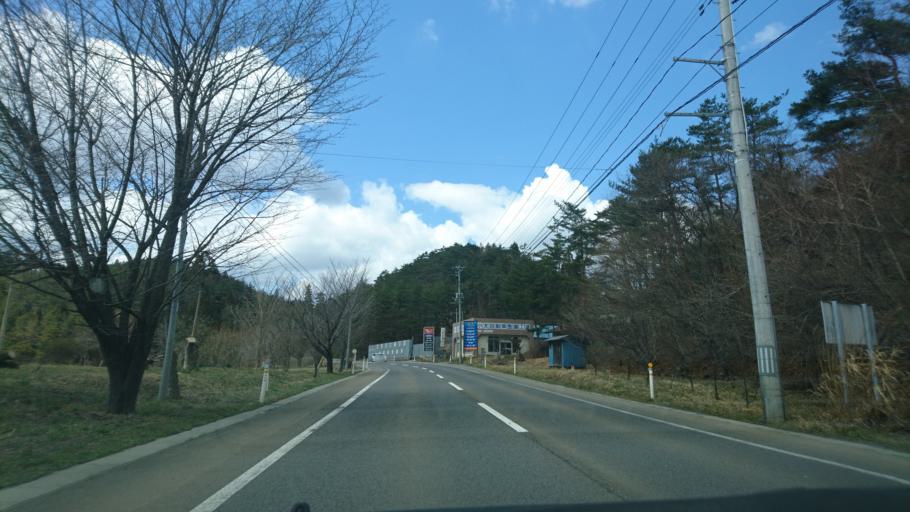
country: JP
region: Iwate
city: Tono
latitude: 39.2790
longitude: 141.4123
